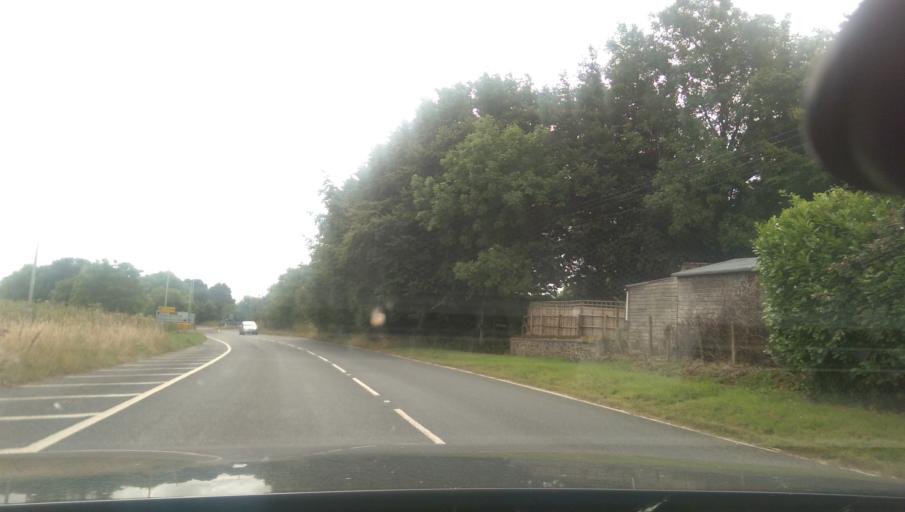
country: GB
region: England
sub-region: Devon
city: Okehampton
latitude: 50.7170
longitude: -3.8626
